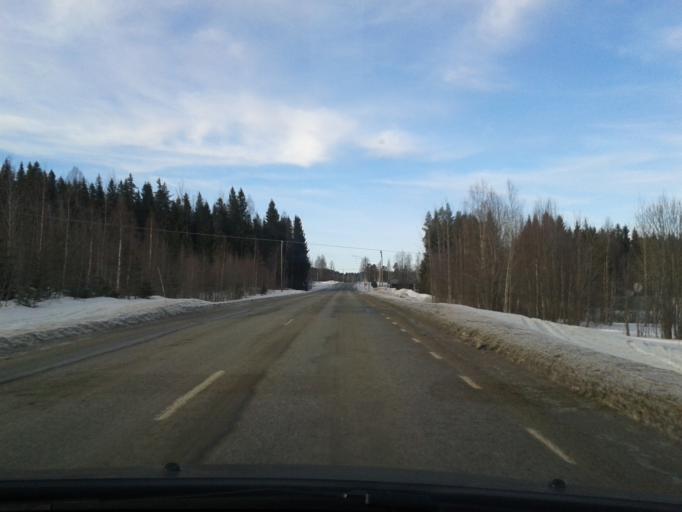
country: SE
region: Vaesternorrland
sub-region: OErnskoeldsviks Kommun
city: Bredbyn
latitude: 63.4737
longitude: 18.0970
